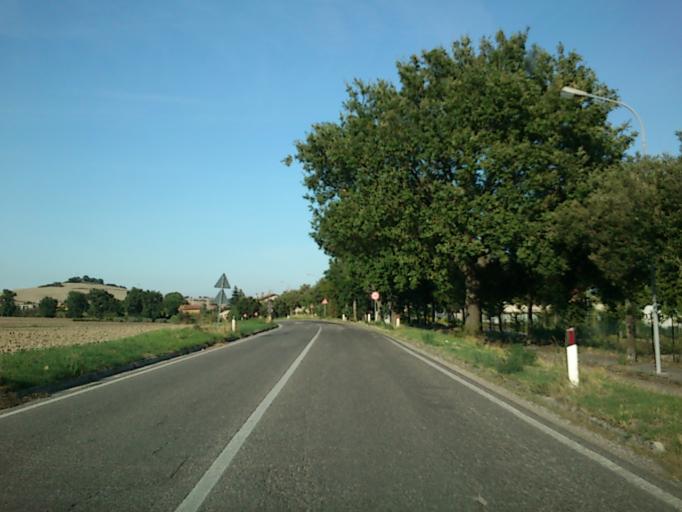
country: IT
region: The Marches
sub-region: Provincia di Pesaro e Urbino
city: Montefelcino
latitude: 43.7079
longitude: 12.8436
